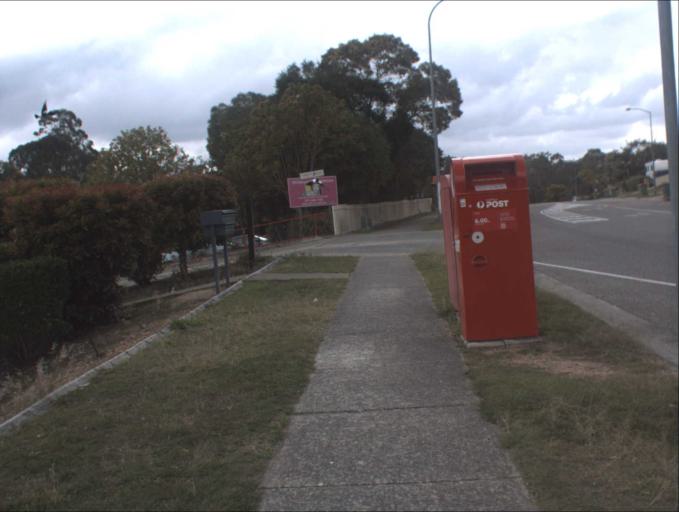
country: AU
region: Queensland
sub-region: Logan
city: Park Ridge South
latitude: -27.6810
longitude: 153.0363
